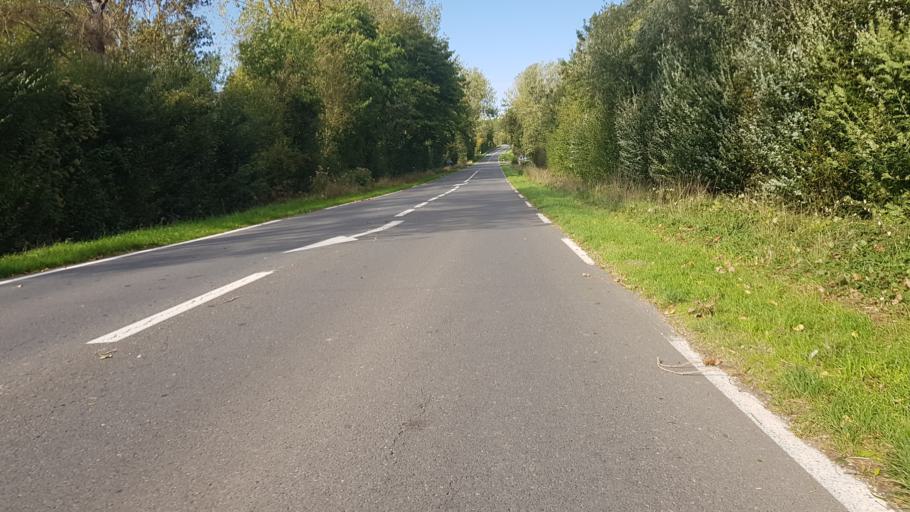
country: FR
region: Poitou-Charentes
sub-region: Departement de la Vienne
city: Chasseneuil-du-Poitou
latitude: 46.6322
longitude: 0.3663
